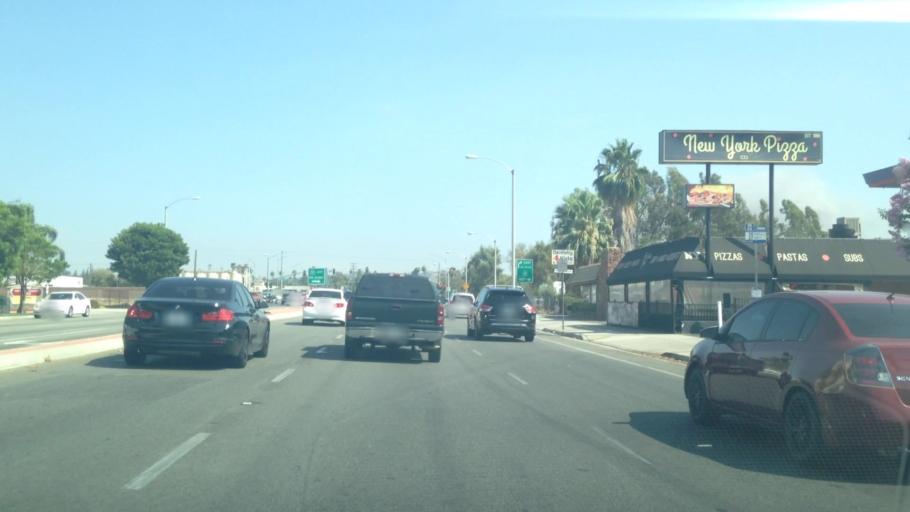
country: US
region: California
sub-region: Riverside County
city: Riverside
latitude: 33.9164
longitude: -117.4443
